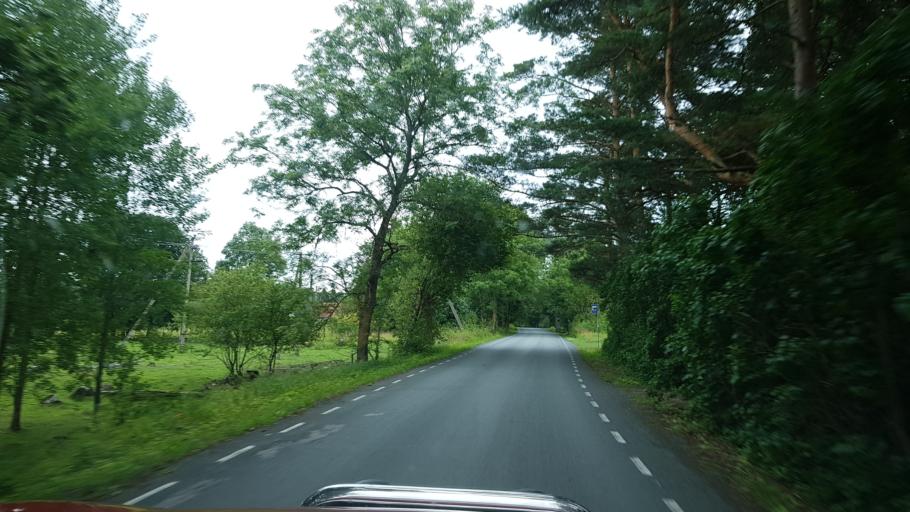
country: EE
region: Laeaene
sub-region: Lihula vald
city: Lihula
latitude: 58.8729
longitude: 23.9067
